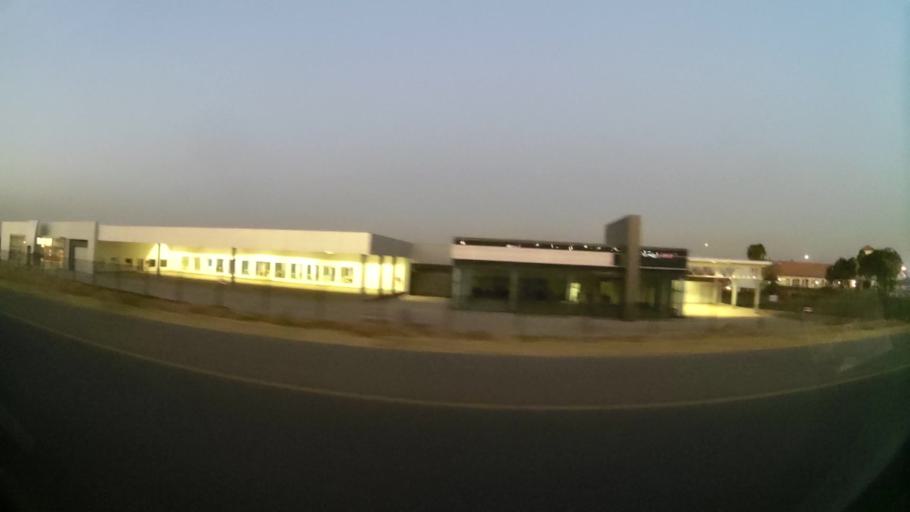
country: ZA
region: North-West
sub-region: Bojanala Platinum District Municipality
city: Rustenburg
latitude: -25.6871
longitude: 27.2538
